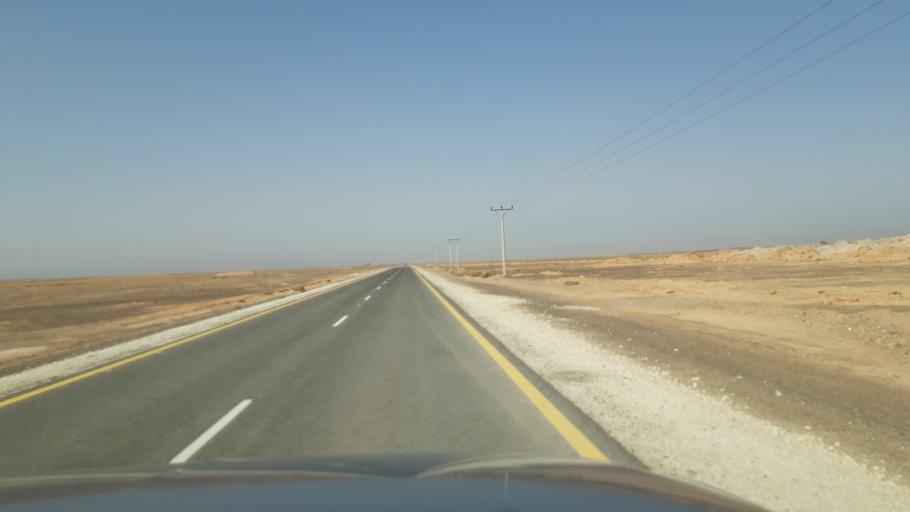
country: JO
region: Amman
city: Al Azraq ash Shamali
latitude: 31.7794
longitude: 36.7852
